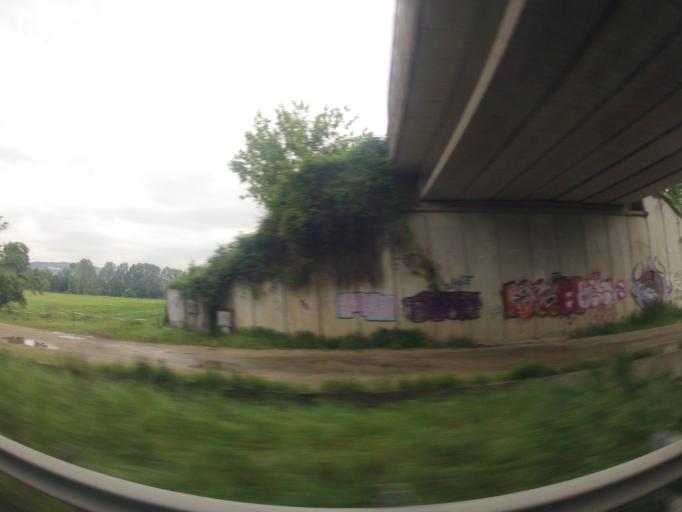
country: IT
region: Piedmont
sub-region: Provincia di Torino
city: La Loggia
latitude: 44.9611
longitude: 7.6795
